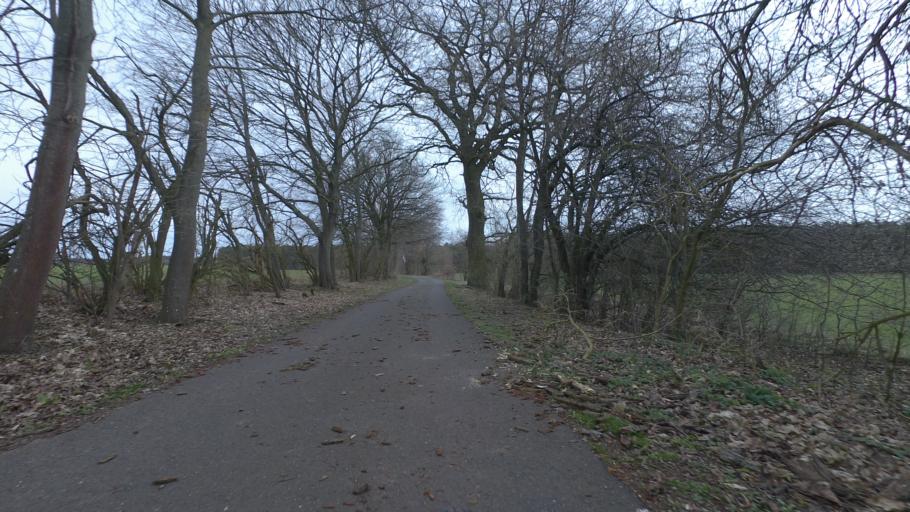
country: DE
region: Brandenburg
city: Neuruppin
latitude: 52.9829
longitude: 12.8619
